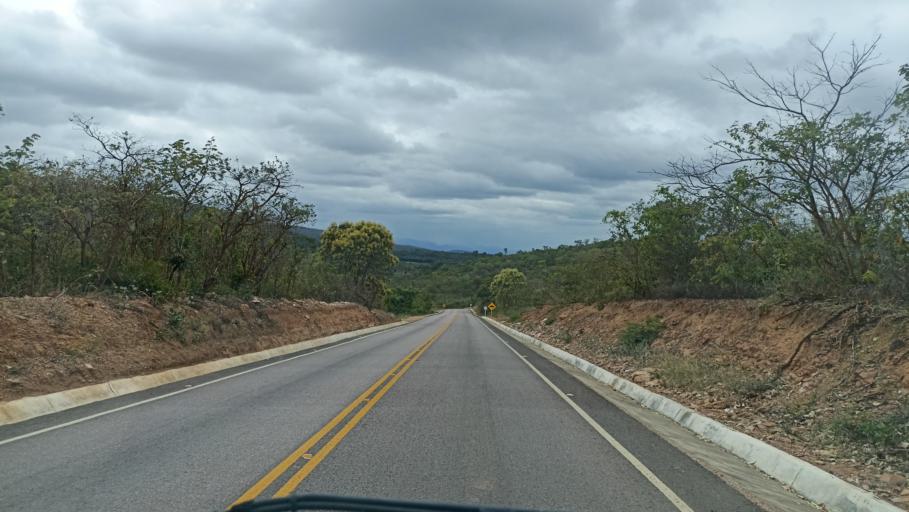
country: BR
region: Bahia
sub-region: Andarai
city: Vera Cruz
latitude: -12.9273
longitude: -41.2307
